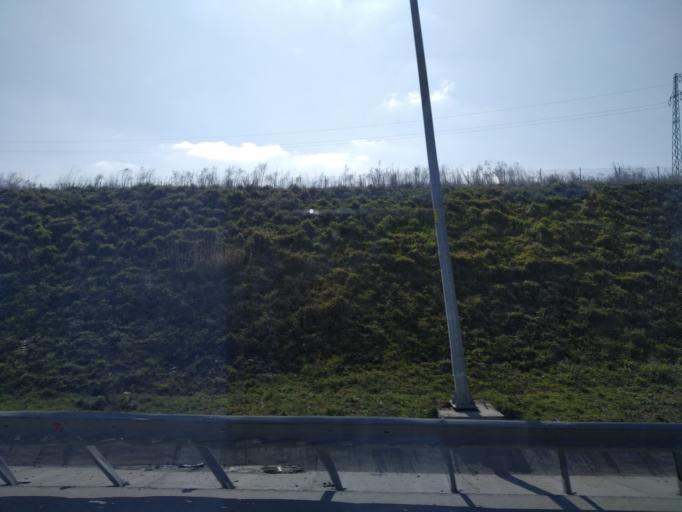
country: TR
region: Istanbul
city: Kemerburgaz
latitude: 41.2302
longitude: 28.8514
